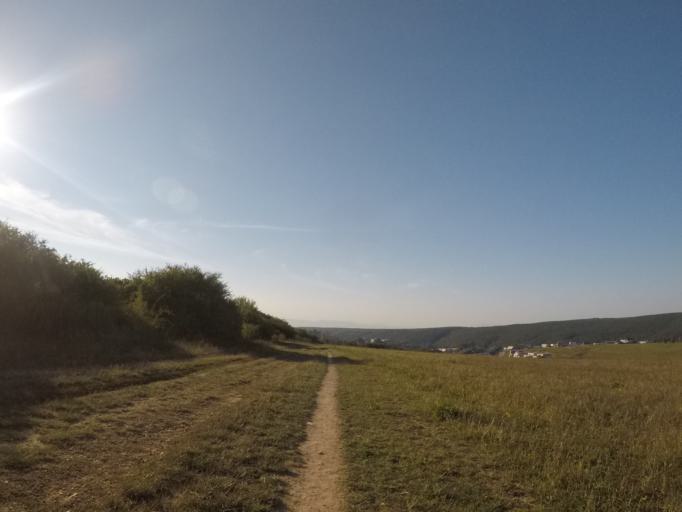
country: SK
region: Kosicky
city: Kosice
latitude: 48.7224
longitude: 21.2036
